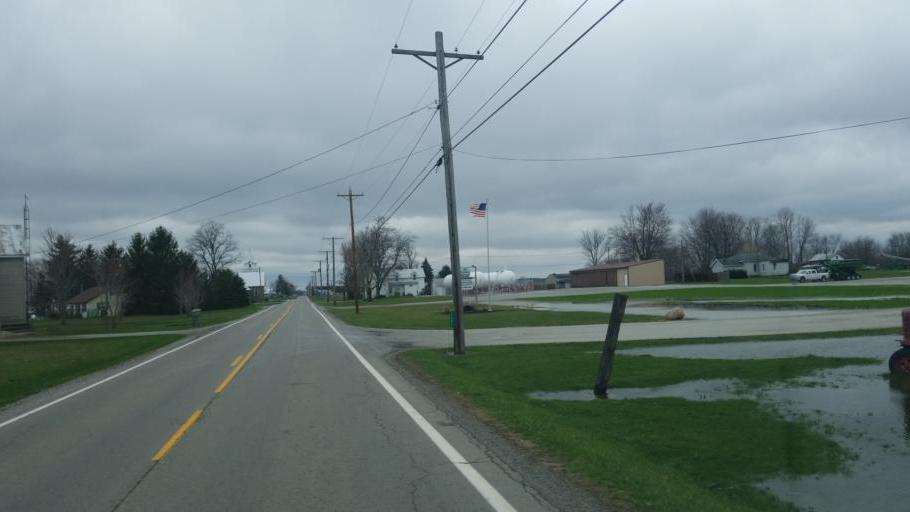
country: US
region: Ohio
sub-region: Hardin County
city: Kenton
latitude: 40.7118
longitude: -83.5671
